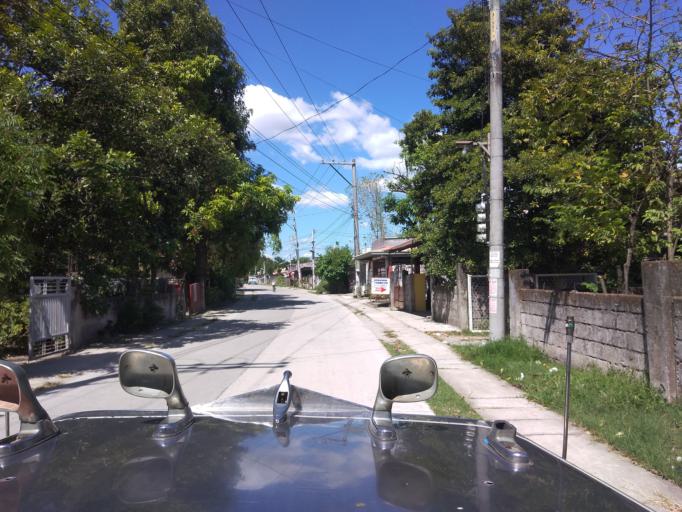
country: PH
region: Central Luzon
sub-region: Province of Pampanga
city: Magliman
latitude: 15.0418
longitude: 120.6447
